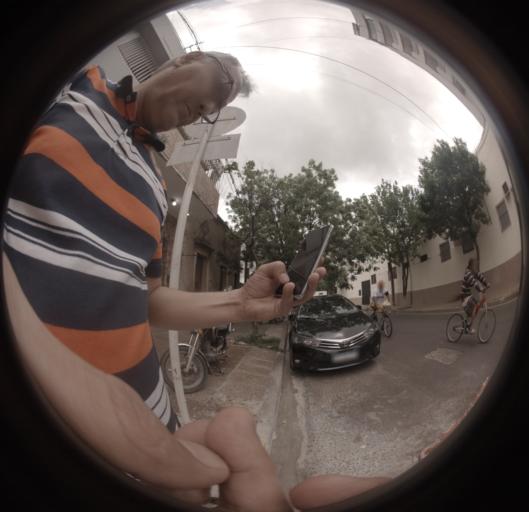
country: AR
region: Corrientes
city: Corrientes
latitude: -27.4701
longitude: -58.8417
